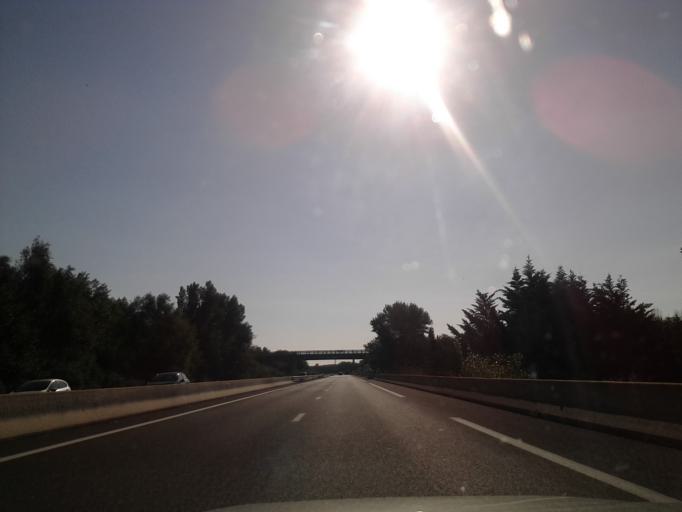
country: FR
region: Languedoc-Roussillon
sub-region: Departement des Pyrenees-Orientales
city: Ille-sur-Tet
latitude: 42.6740
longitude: 2.6132
